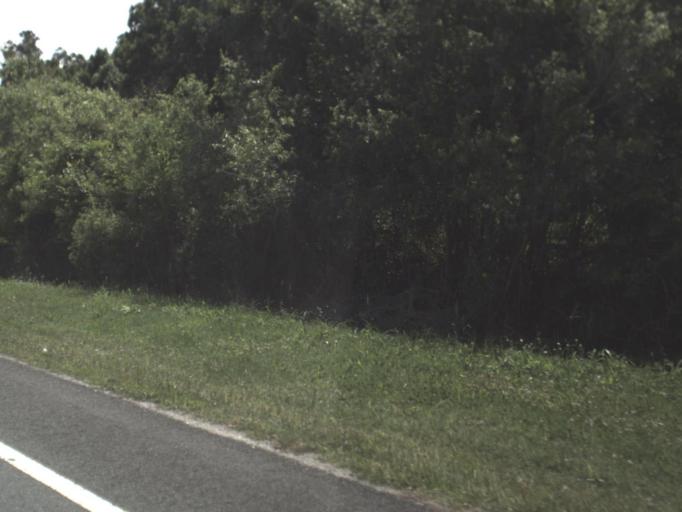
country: US
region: Florida
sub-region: Duval County
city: Jacksonville
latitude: 30.4422
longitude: -81.6410
